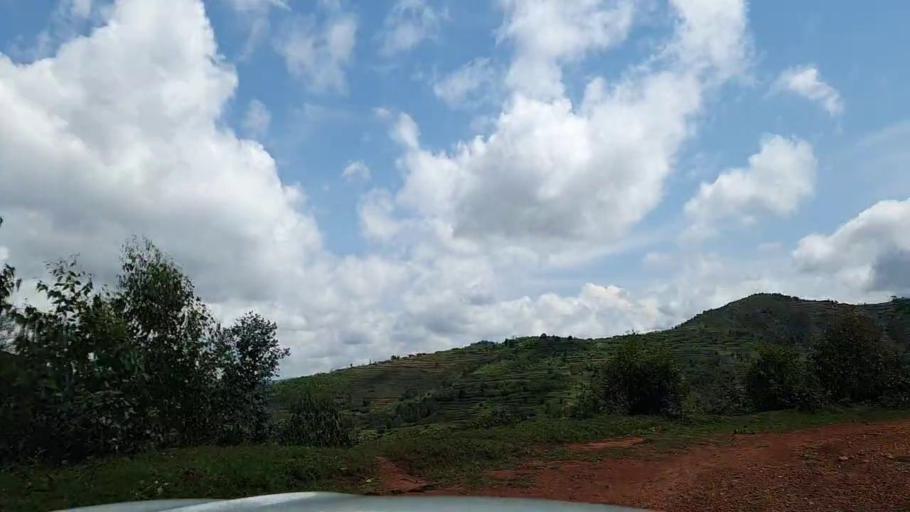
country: RW
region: Southern Province
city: Gikongoro
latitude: -2.3609
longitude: 29.5431
